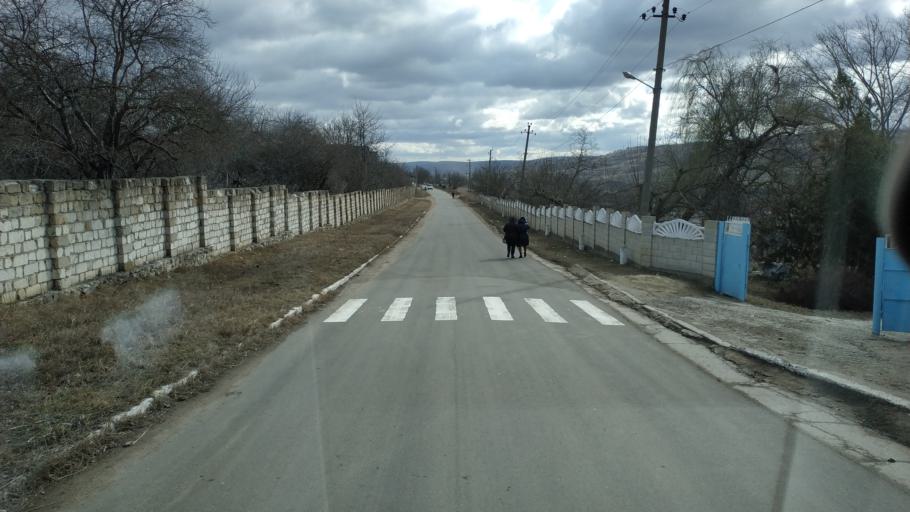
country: MD
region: Stinga Nistrului
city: Bucovat
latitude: 47.2271
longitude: 28.4352
